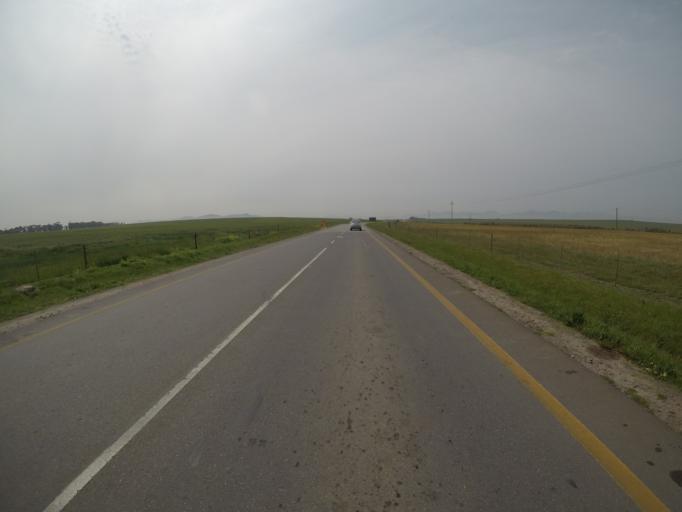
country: ZA
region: Western Cape
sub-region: City of Cape Town
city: Kraaifontein
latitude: -33.6976
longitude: 18.7074
